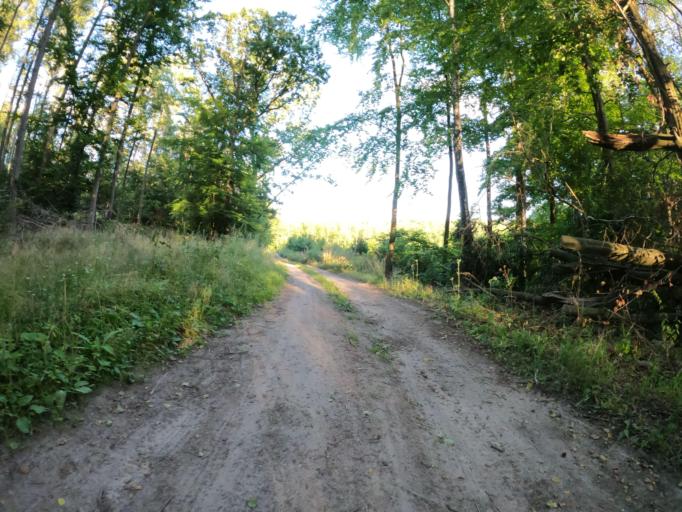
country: PL
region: West Pomeranian Voivodeship
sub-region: Powiat drawski
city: Drawsko Pomorskie
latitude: 53.6479
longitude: 15.9083
